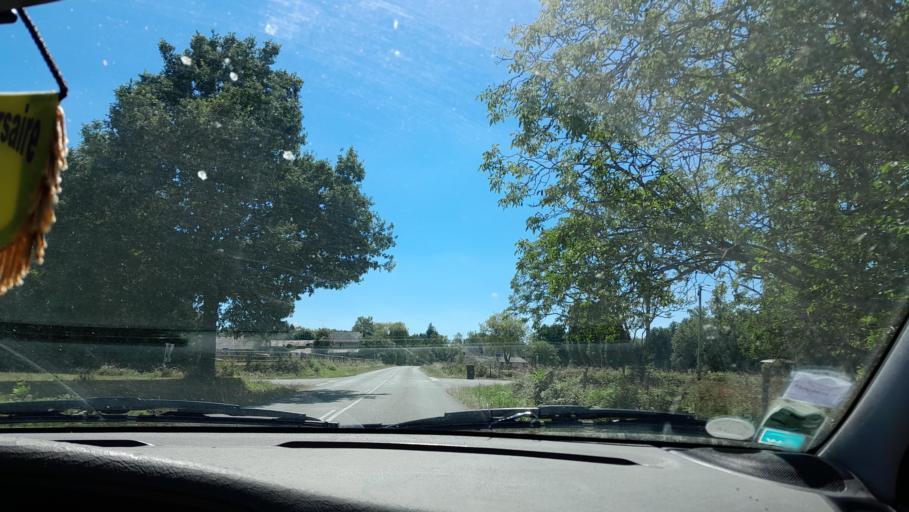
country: FR
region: Pays de la Loire
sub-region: Departement de la Mayenne
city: Ballots
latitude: 47.8905
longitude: -1.1161
